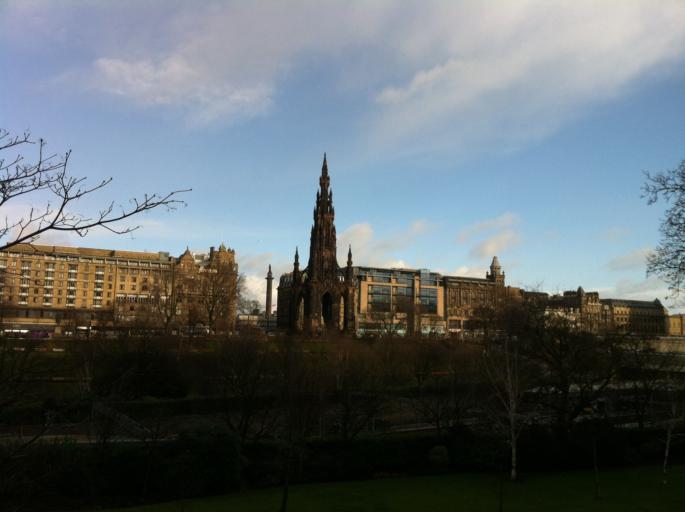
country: GB
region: Scotland
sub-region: Edinburgh
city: Edinburgh
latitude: 55.9506
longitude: -3.1939
